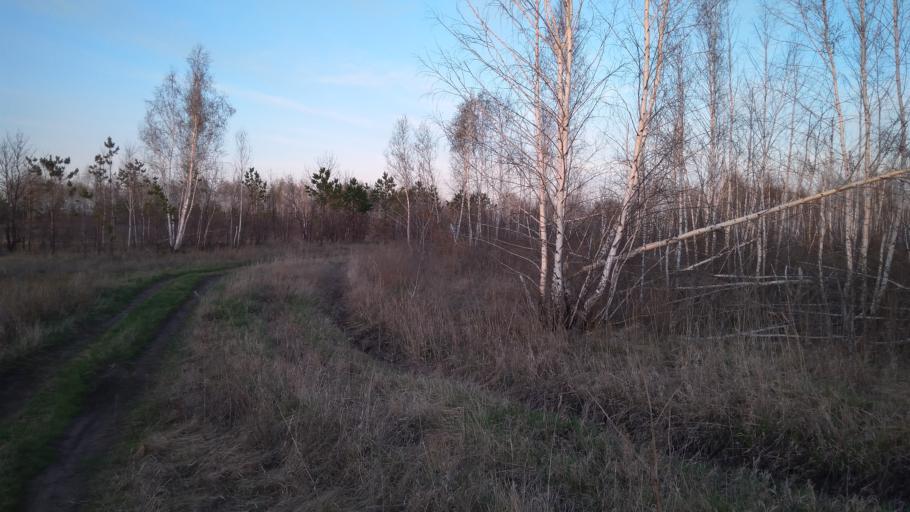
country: RU
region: Chelyabinsk
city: Bobrovka
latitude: 54.0616
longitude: 61.6890
